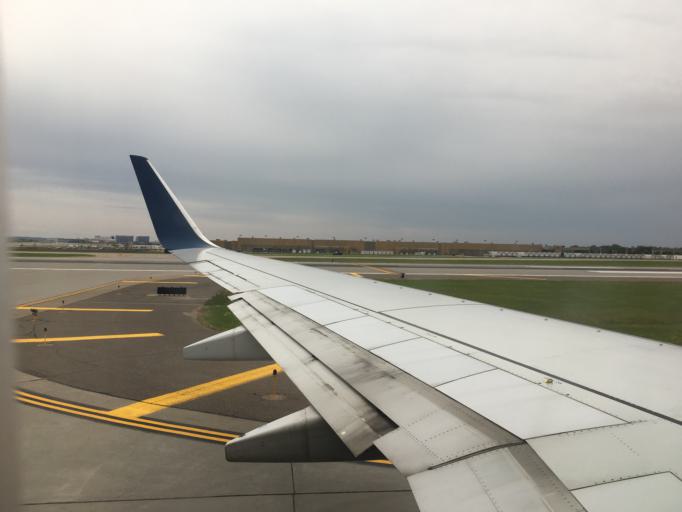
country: US
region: Minnesota
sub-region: Hennepin County
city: Richfield
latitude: 44.8862
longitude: -93.2273
